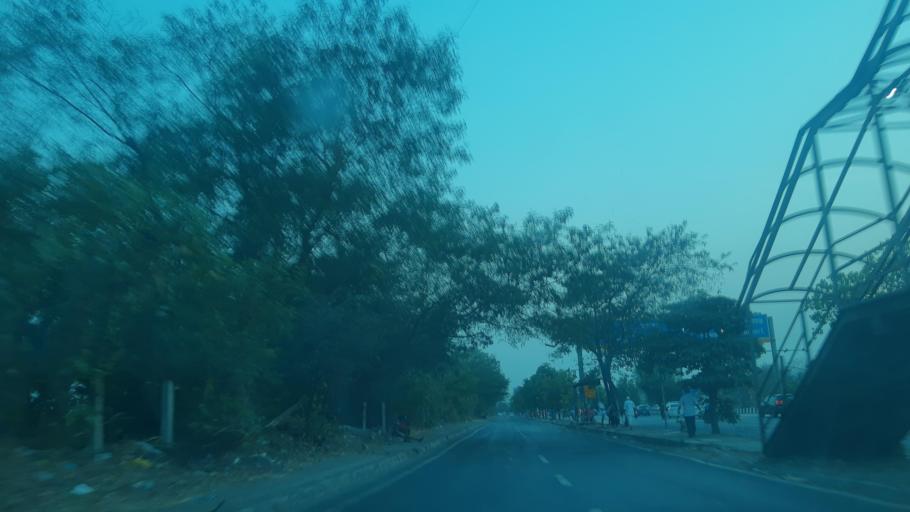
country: IN
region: Maharashtra
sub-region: Mumbai Suburban
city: Powai
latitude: 19.1304
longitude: 72.9422
